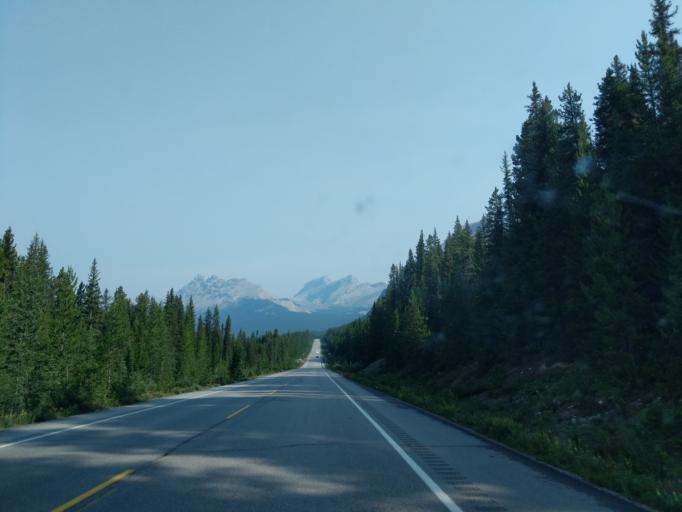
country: CA
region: Alberta
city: Lake Louise
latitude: 51.5994
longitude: -116.3083
